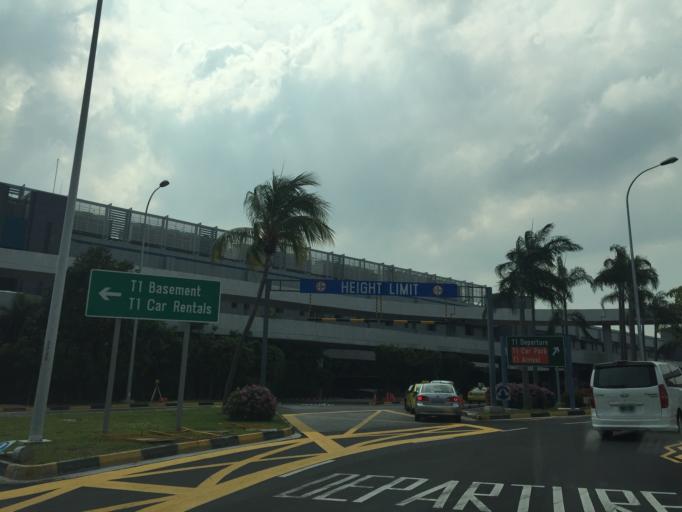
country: SG
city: Singapore
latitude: 1.3600
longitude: 103.9885
